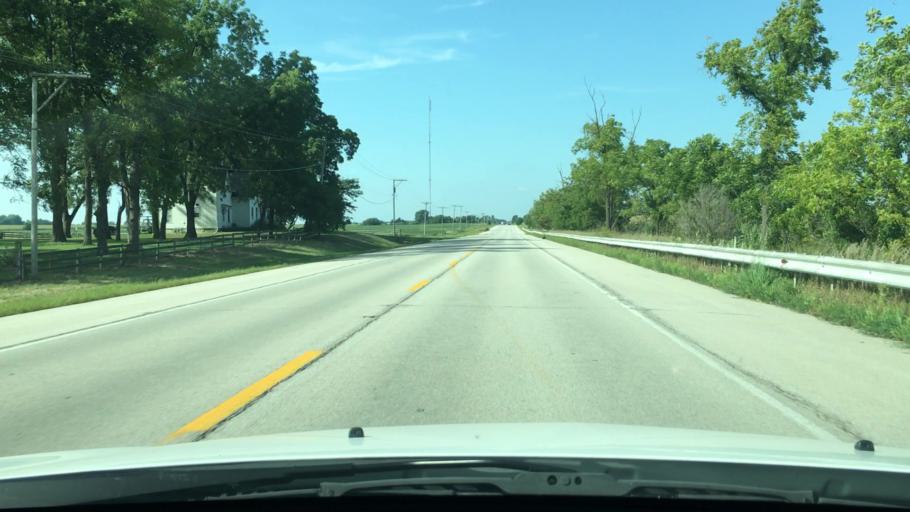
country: US
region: Illinois
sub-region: DeKalb County
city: DeKalb
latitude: 41.8660
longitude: -88.7538
